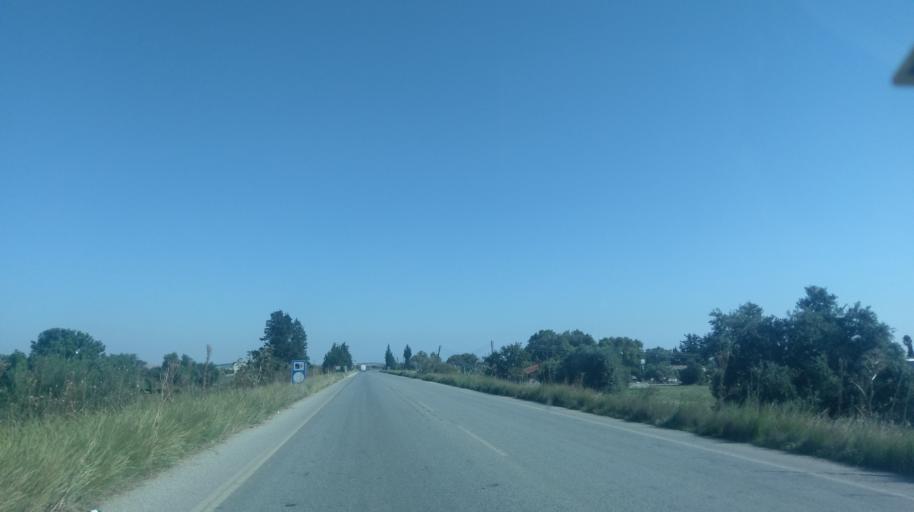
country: CY
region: Ammochostos
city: Lefkonoiko
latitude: 35.2622
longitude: 33.7827
